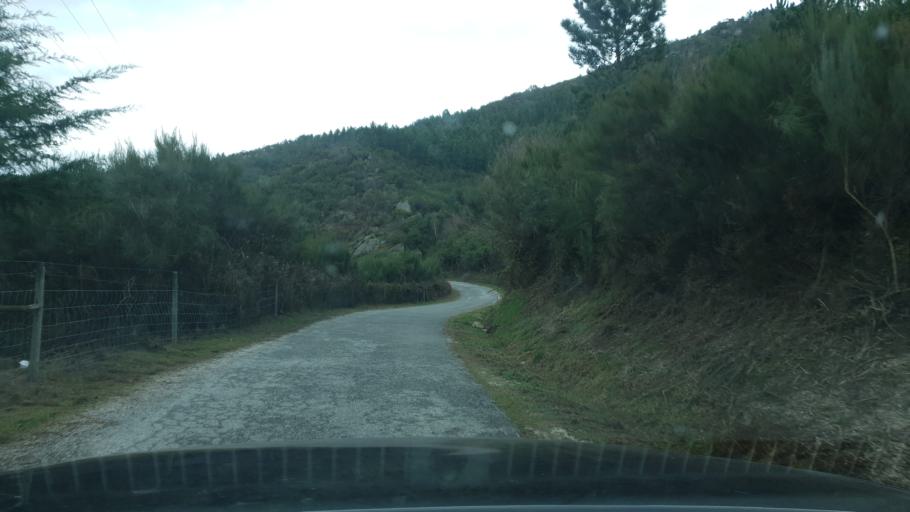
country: PT
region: Viseu
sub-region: Castro Daire
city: Castro Daire
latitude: 40.8767
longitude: -7.9901
